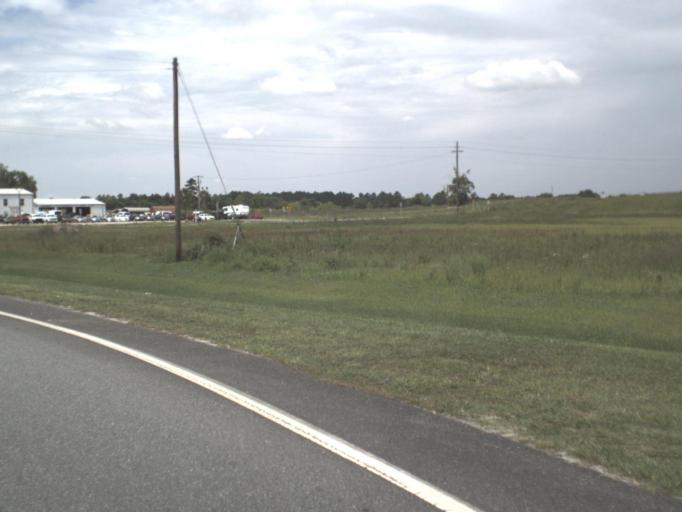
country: US
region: Florida
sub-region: Suwannee County
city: Live Oak
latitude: 30.3197
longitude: -82.9698
